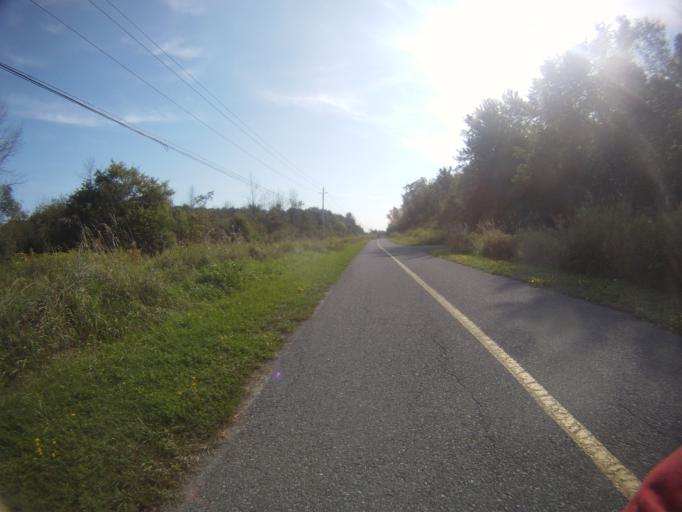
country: CA
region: Ontario
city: Bells Corners
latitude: 45.3400
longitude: -75.8709
